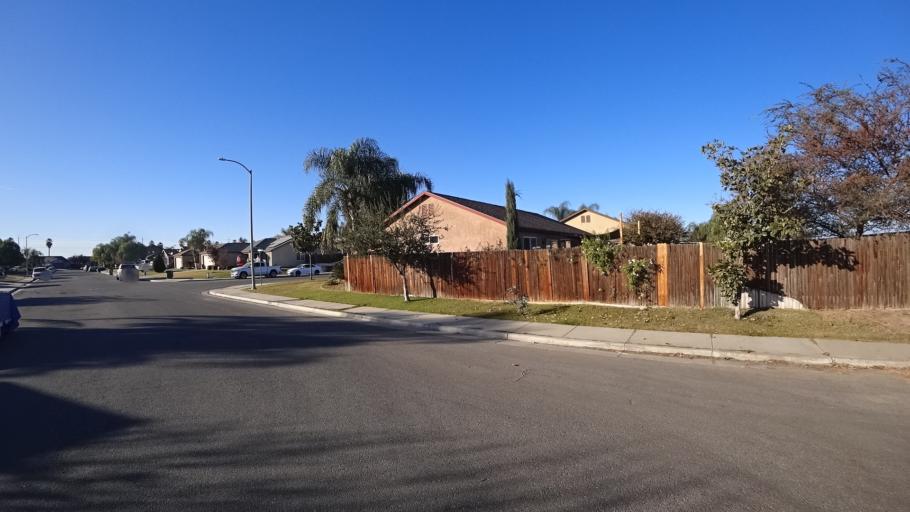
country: US
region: California
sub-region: Kern County
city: Greenfield
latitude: 35.2784
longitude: -118.9994
